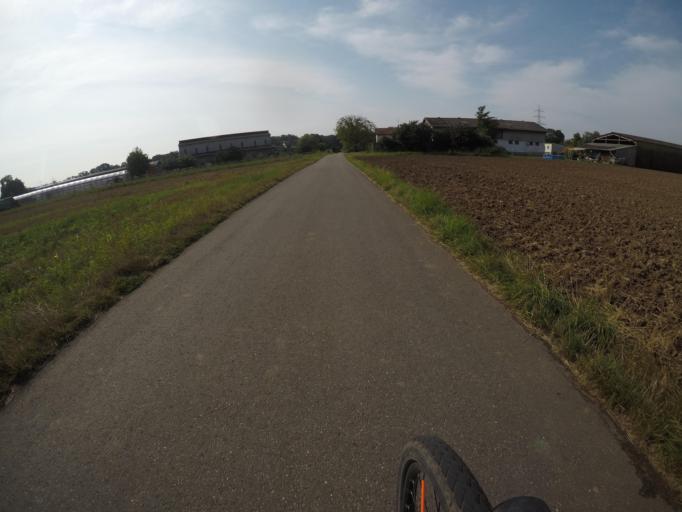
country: DE
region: Baden-Wuerttemberg
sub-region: Karlsruhe Region
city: Plankstadt
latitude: 49.4268
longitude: 8.5717
